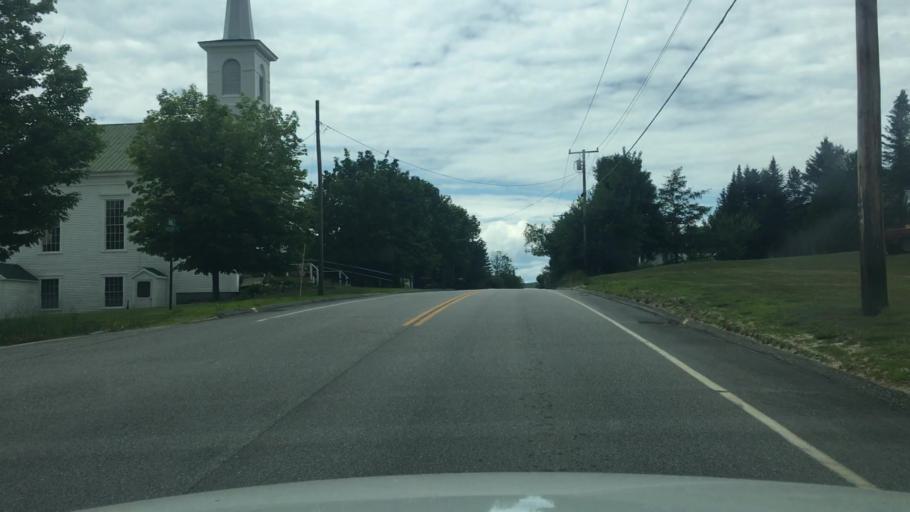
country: US
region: Maine
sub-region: Oxford County
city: Hartford
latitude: 44.3661
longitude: -70.4599
